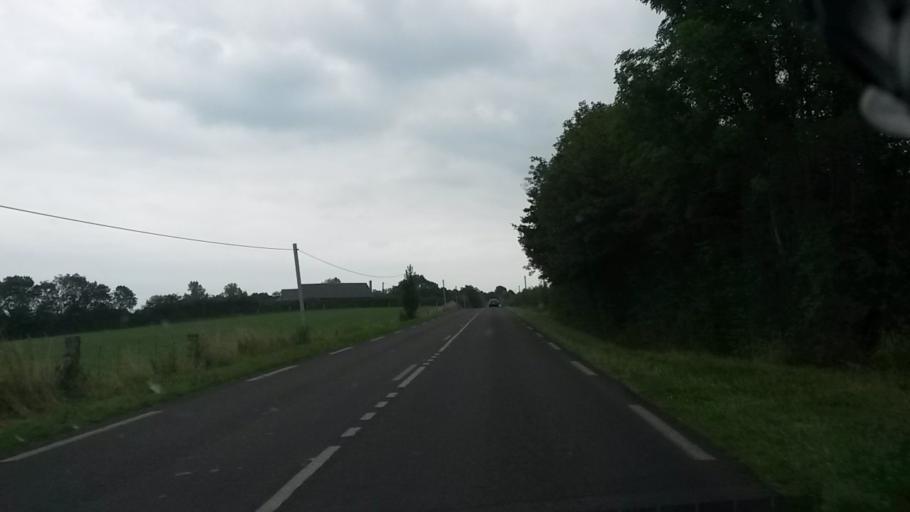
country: FR
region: Haute-Normandie
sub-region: Departement de la Seine-Maritime
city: Gaillefontaine
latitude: 49.6454
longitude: 1.6161
